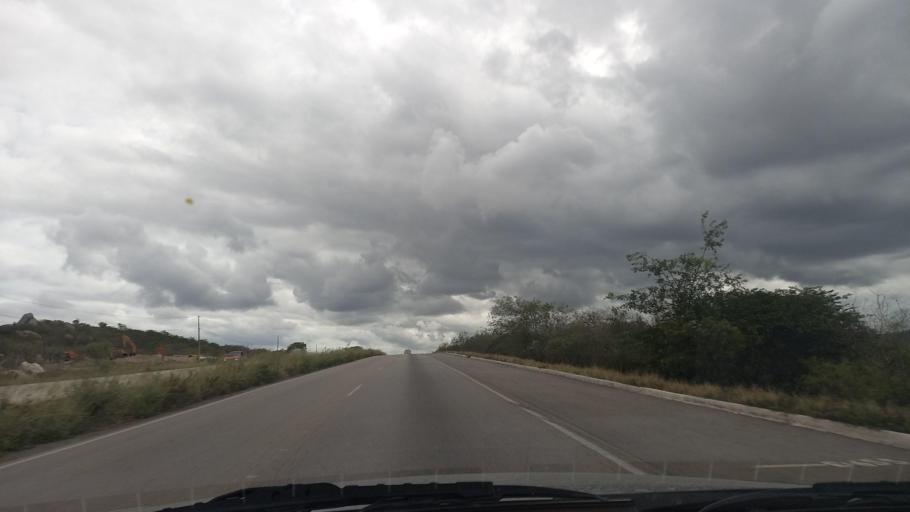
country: BR
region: Pernambuco
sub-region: Caruaru
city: Caruaru
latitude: -8.3235
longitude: -36.1044
